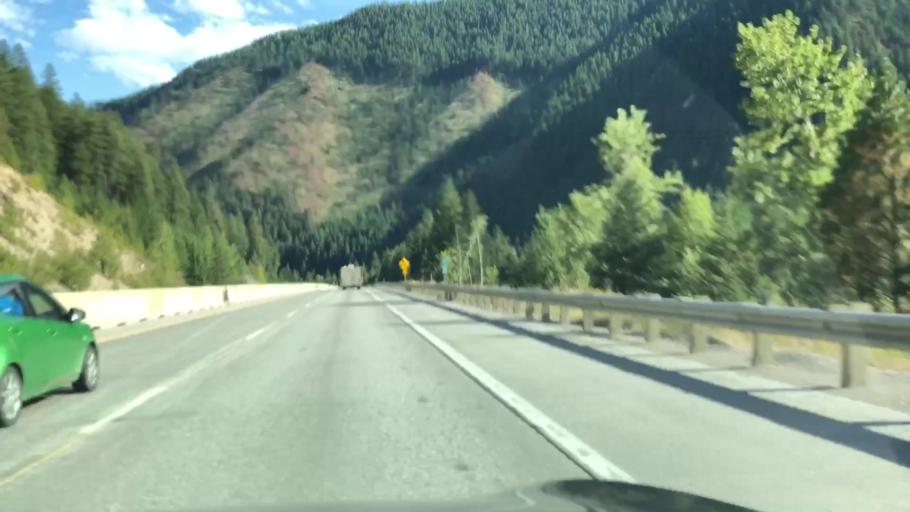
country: US
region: Montana
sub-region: Sanders County
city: Thompson Falls
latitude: 47.3056
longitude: -115.2046
